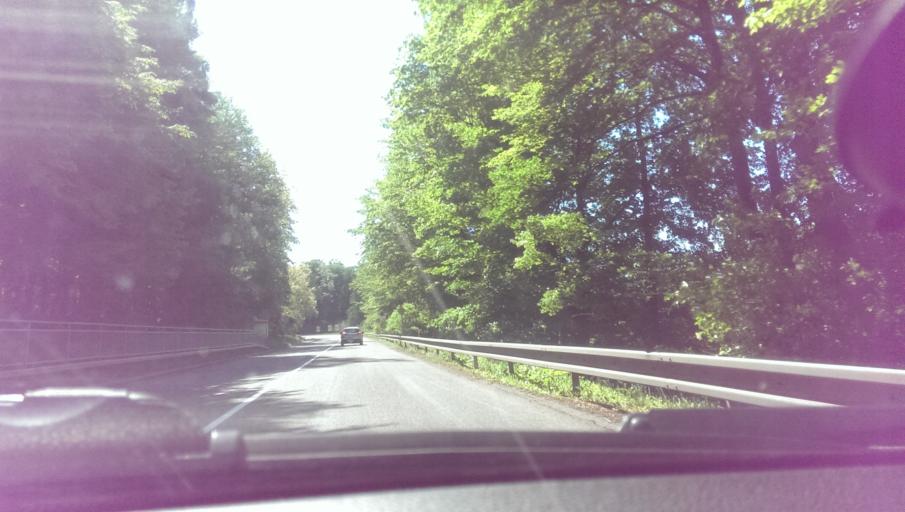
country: CZ
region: Zlin
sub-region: Okres Zlin
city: Zlin
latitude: 49.2099
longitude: 17.6611
